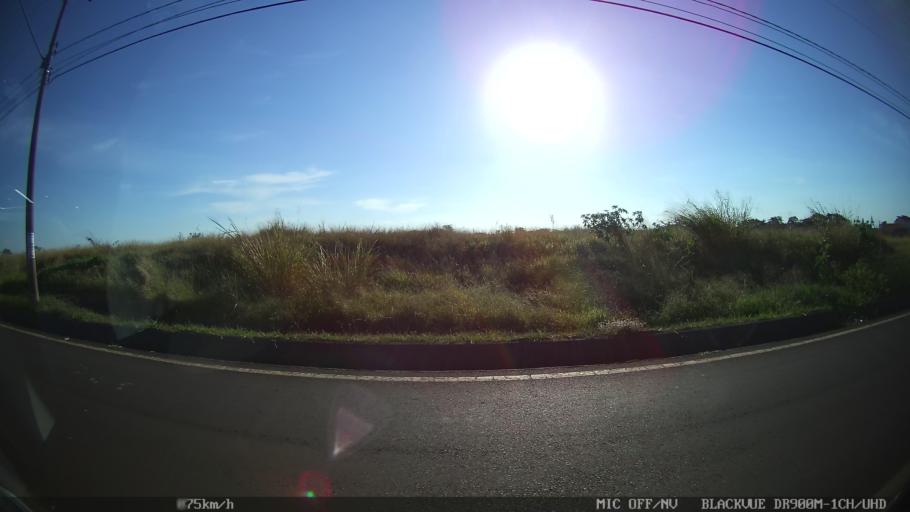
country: BR
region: Sao Paulo
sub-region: Franca
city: Franca
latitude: -20.5064
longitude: -47.3718
